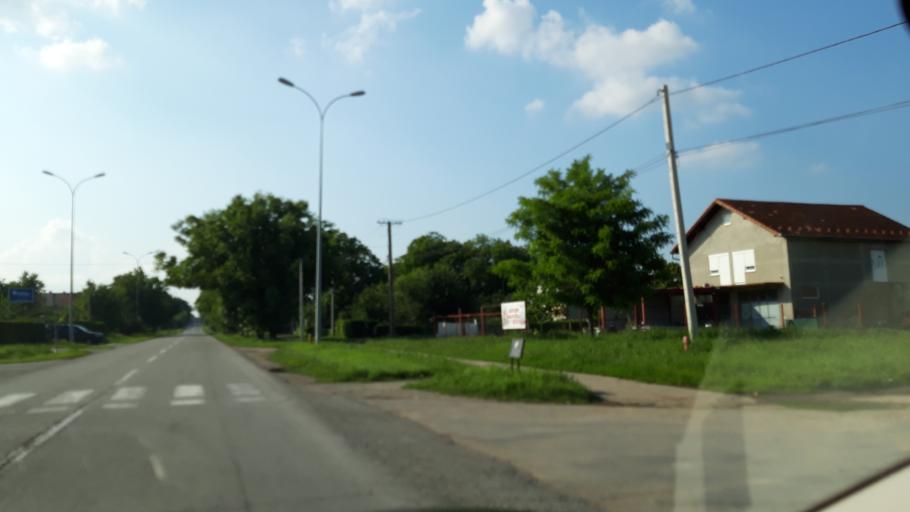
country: RS
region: Autonomna Pokrajina Vojvodina
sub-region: Sremski Okrug
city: Ingija
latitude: 45.0324
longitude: 20.0983
